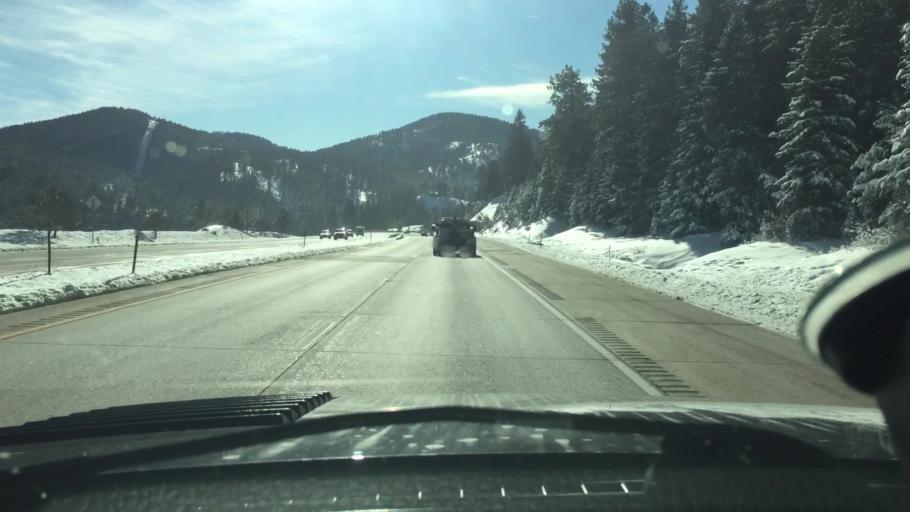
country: US
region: Colorado
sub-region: Jefferson County
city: Indian Hills
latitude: 39.5980
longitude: -105.2258
